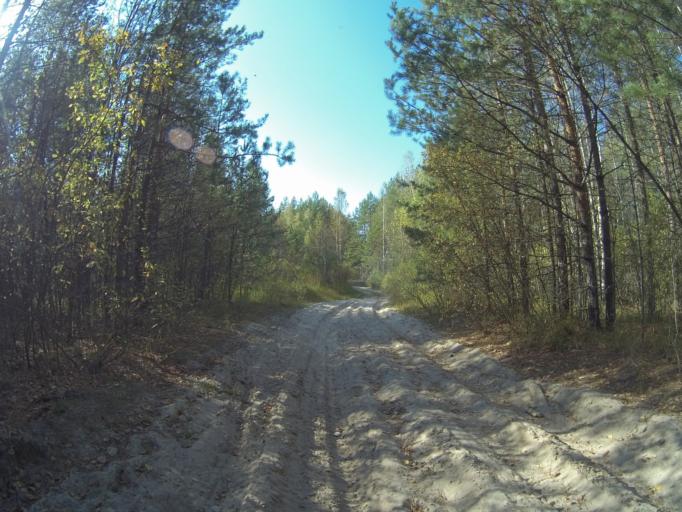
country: RU
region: Vladimir
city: Sobinka
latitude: 55.9265
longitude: 40.0770
